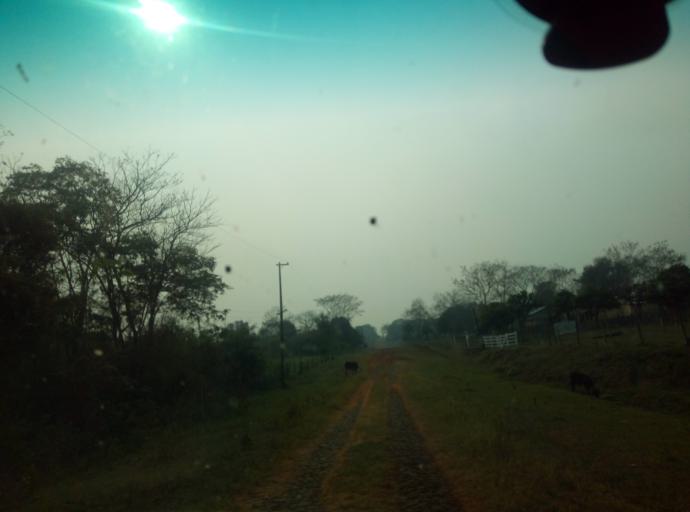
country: PY
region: Caaguazu
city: Carayao
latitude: -25.2038
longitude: -56.2348
